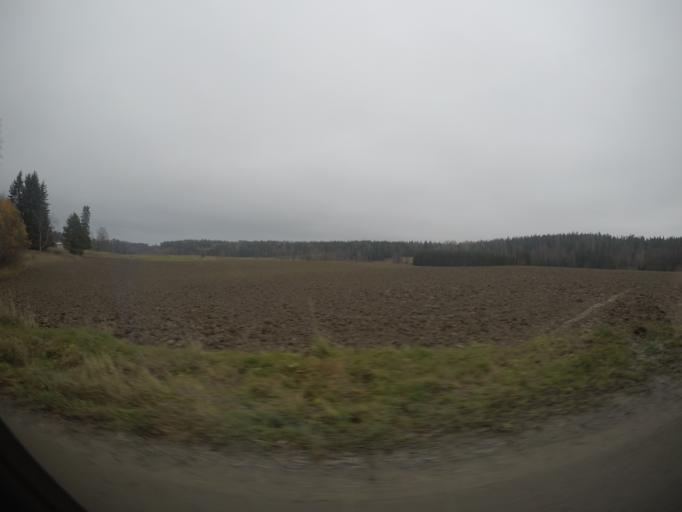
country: SE
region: Vaestmanland
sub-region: Surahammars Kommun
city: Ramnas
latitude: 59.7427
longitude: 16.1418
